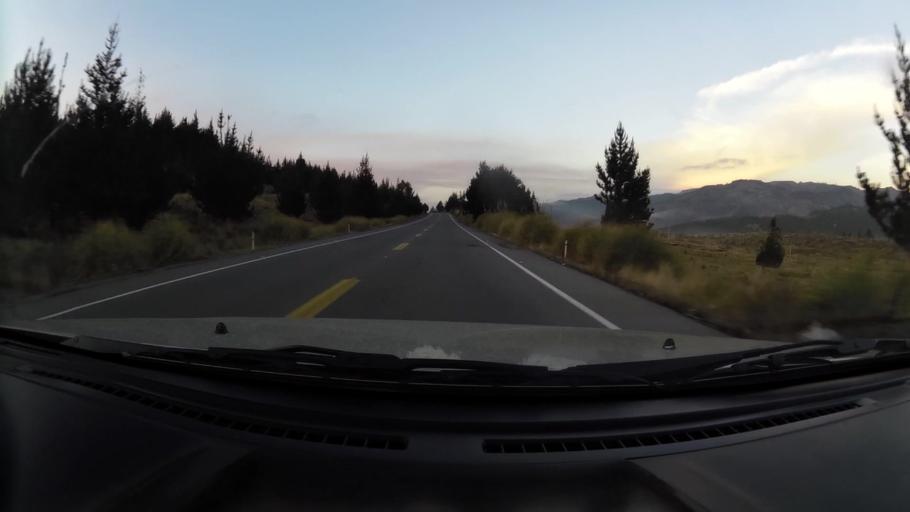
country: EC
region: Chimborazo
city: Alausi
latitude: -2.0423
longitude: -78.7384
